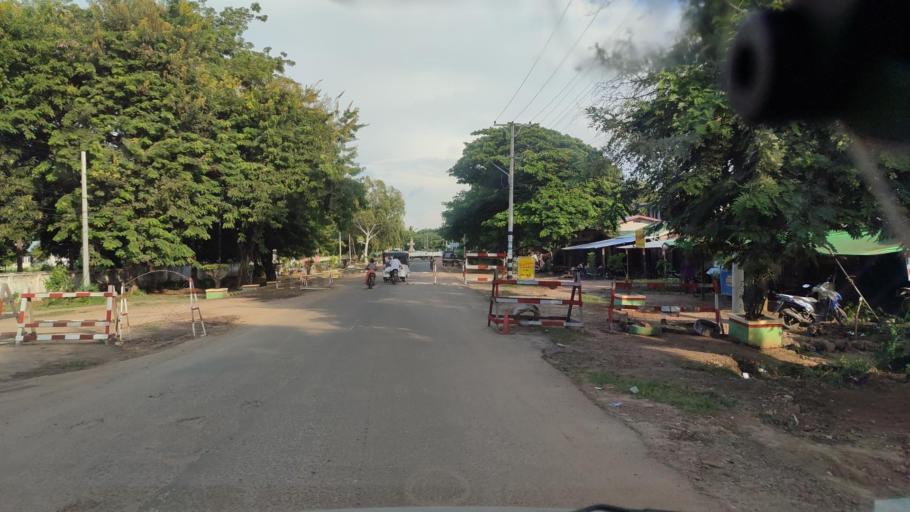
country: MM
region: Magway
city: Chauk
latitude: 20.8341
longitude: 95.1408
